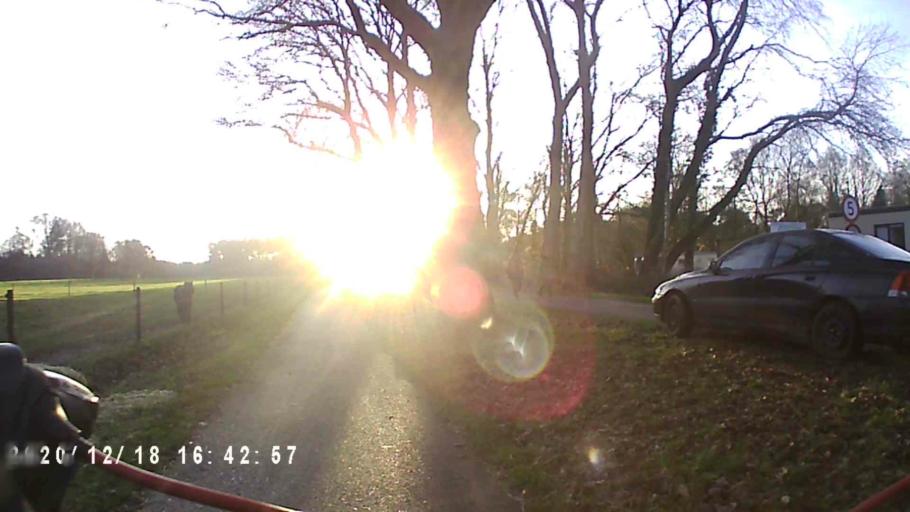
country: NL
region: Drenthe
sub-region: Gemeente Tynaarlo
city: Zuidlaren
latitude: 53.0801
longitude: 6.6671
